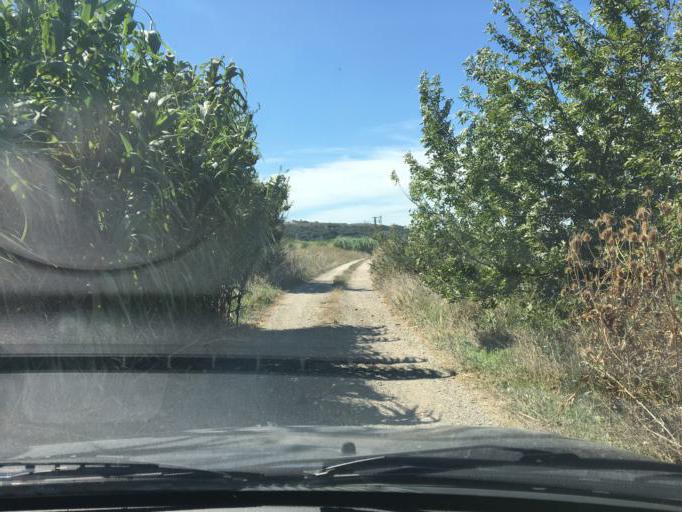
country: FR
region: Provence-Alpes-Cote d'Azur
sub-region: Departement du Vaucluse
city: Caderousse
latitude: 44.0945
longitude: 4.7861
